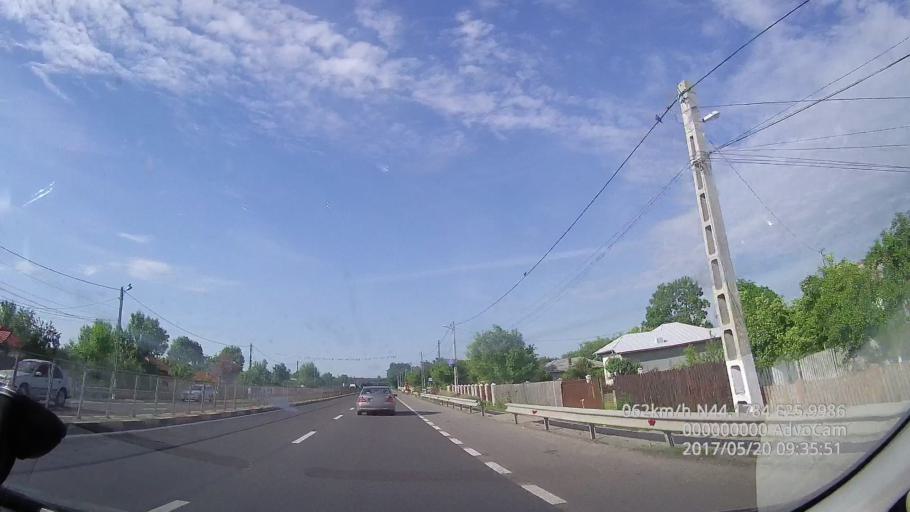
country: RO
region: Giurgiu
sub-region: Comuna Calugareni
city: Calugareni
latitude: 44.1782
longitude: 25.9985
